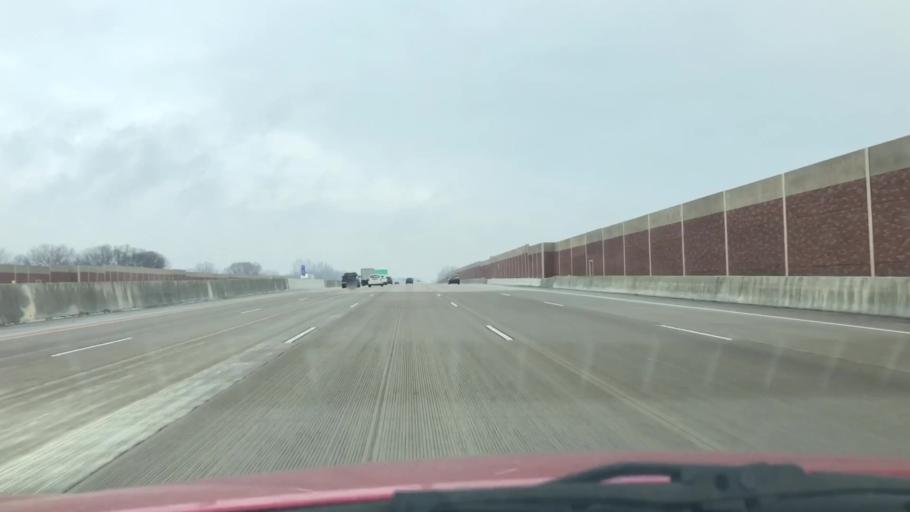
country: US
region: Wisconsin
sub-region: Brown County
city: Ashwaubenon
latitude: 44.4942
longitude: -88.0812
